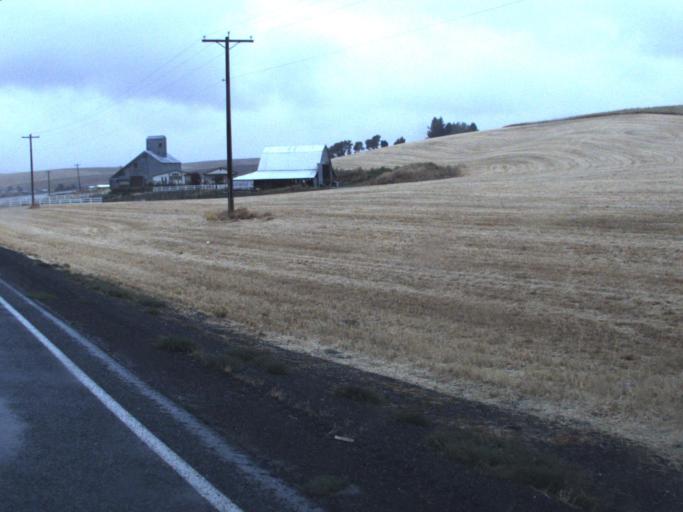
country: US
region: Washington
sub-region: Whitman County
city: Colfax
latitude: 47.0708
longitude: -117.5335
